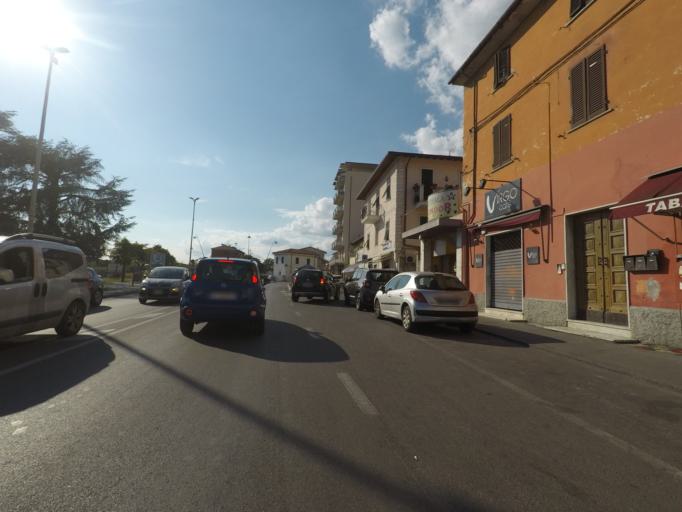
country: IT
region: Tuscany
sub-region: Provincia di Massa-Carrara
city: Massa
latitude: 44.0243
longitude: 10.1372
